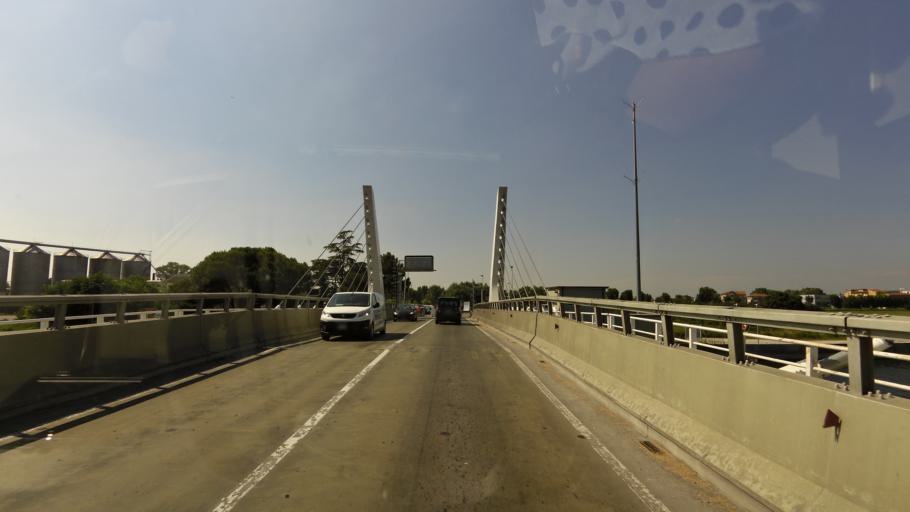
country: IT
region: Emilia-Romagna
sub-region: Provincia di Ravenna
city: Ravenna
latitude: 44.4289
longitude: 12.2256
